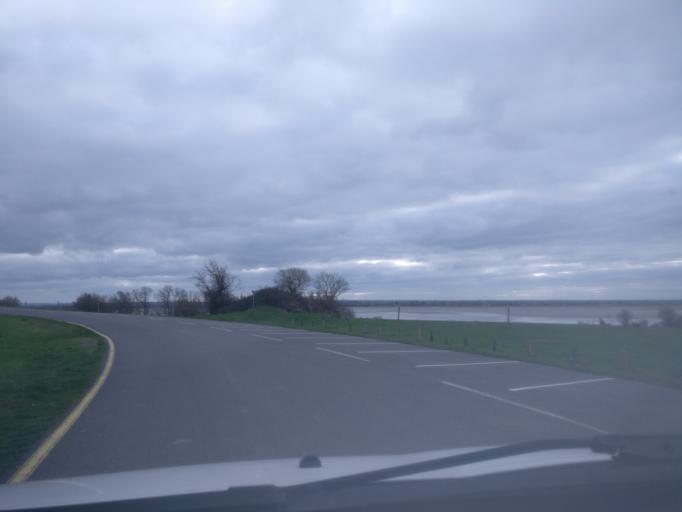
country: FR
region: Lower Normandy
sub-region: Departement de la Manche
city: Marcey-les-Greves
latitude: 48.6564
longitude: -1.4446
